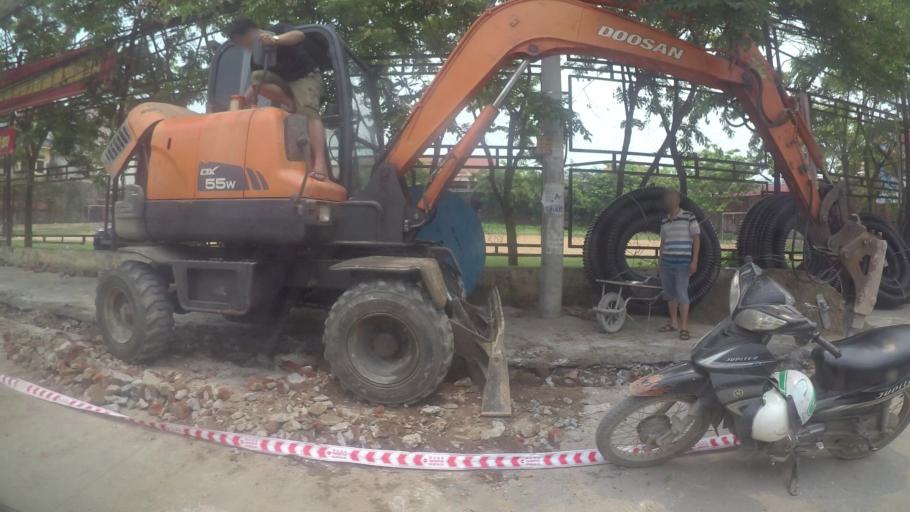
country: VN
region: Ha Noi
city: Ha Dong
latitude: 20.9799
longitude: 105.7486
